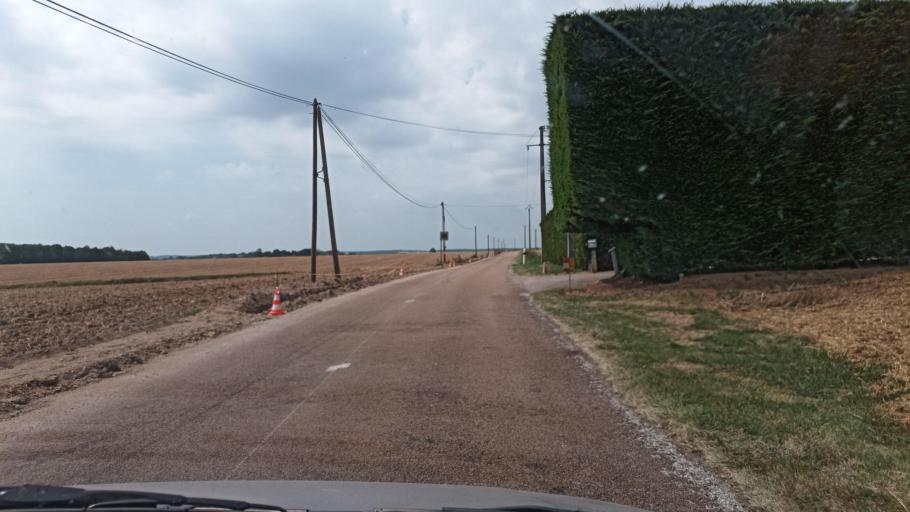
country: FR
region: Bourgogne
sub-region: Departement de l'Yonne
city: Egriselles-le-Bocage
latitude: 48.0465
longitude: 3.2131
